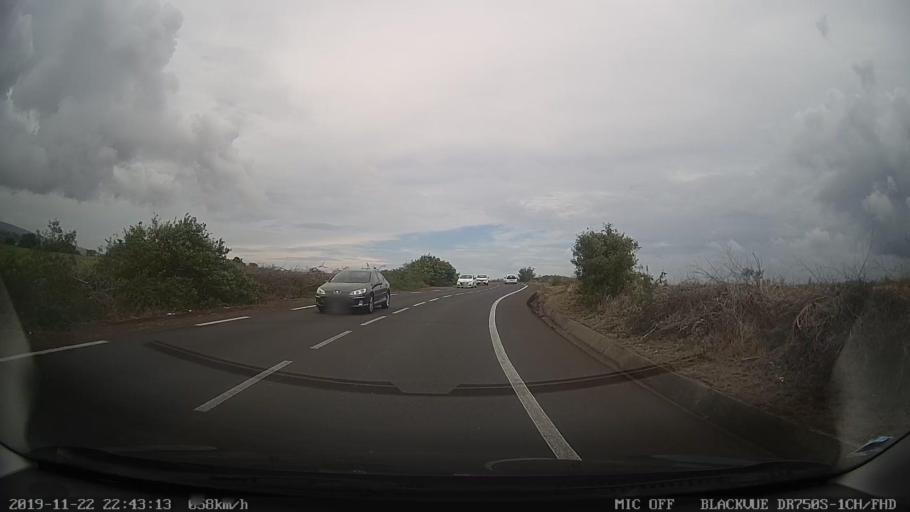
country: RE
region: Reunion
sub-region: Reunion
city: Saint-Paul
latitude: -21.0644
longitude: 55.2363
